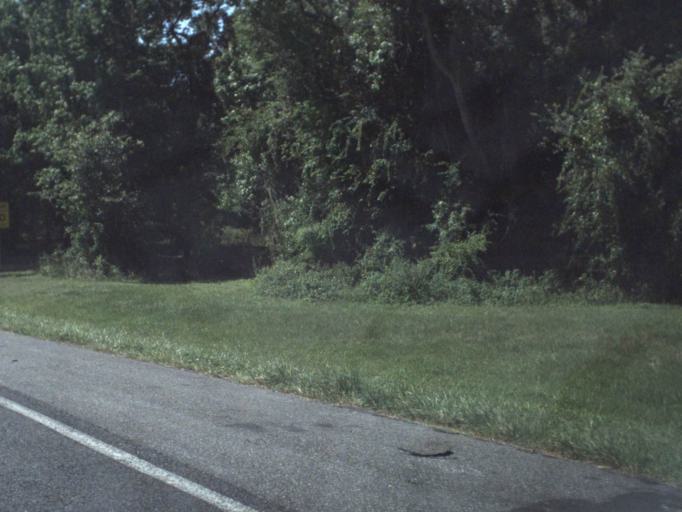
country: US
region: Florida
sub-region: Alachua County
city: Gainesville
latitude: 29.5946
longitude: -82.3668
